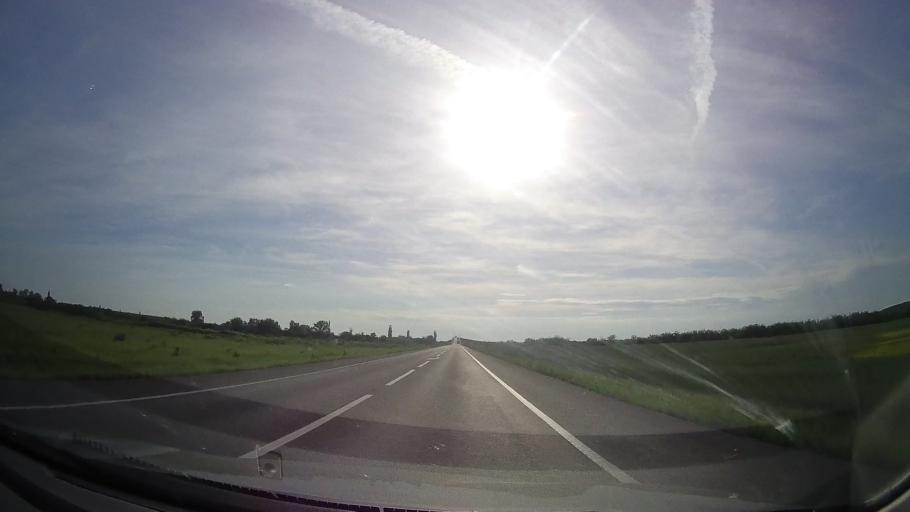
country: RO
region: Timis
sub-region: Municipiul Lugoj
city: Lugoj
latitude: 45.7219
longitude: 21.8888
